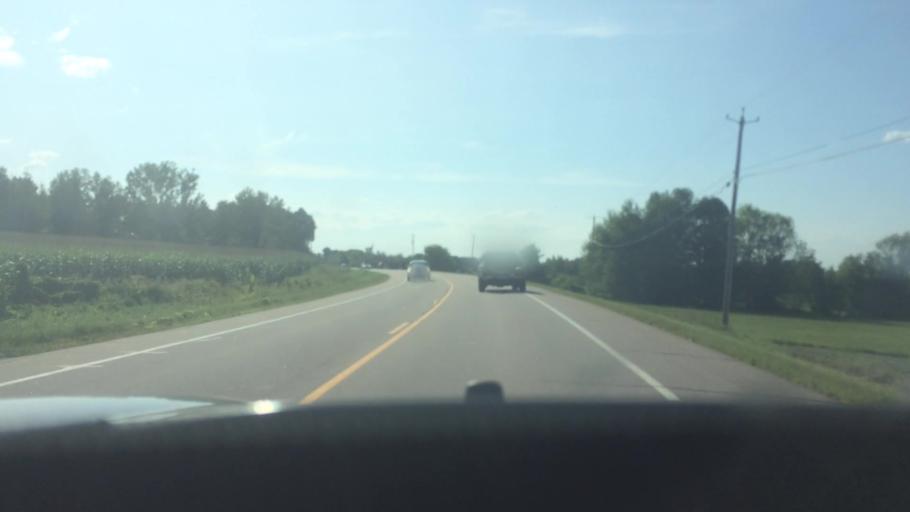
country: US
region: New York
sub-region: Franklin County
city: Malone
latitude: 44.8592
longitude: -74.2439
